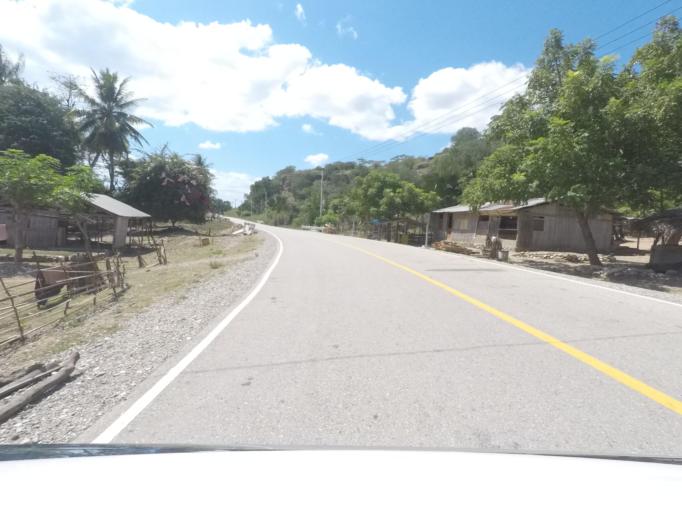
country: TL
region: Lautem
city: Lospalos
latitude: -8.4170
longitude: 126.7961
